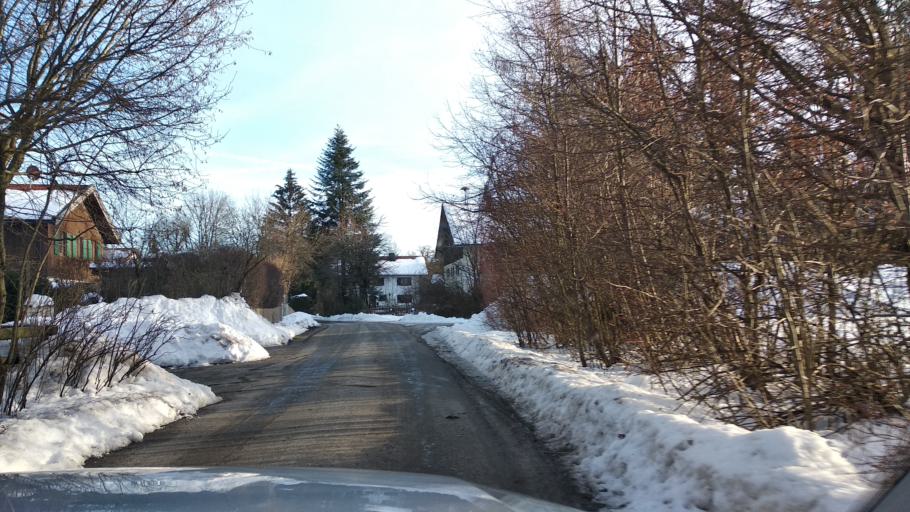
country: DE
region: Bavaria
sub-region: Upper Bavaria
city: Kirchseeon
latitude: 48.0707
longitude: 11.8678
